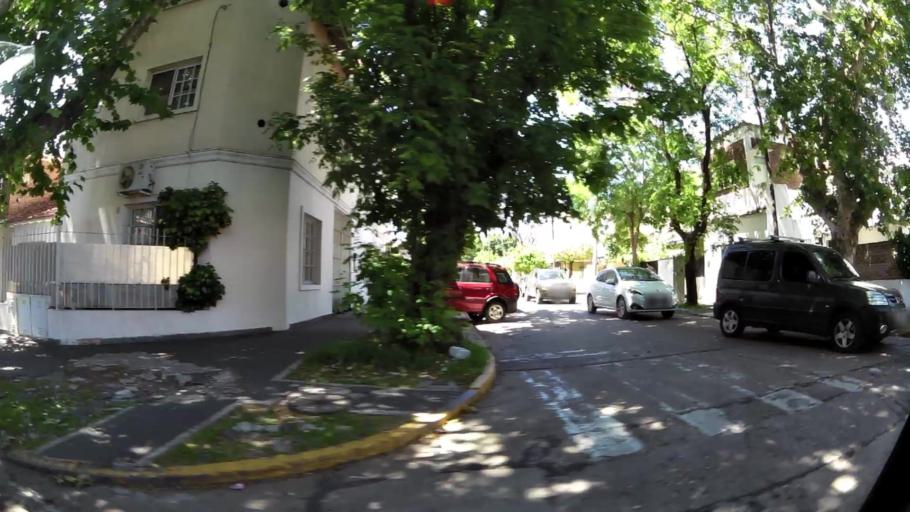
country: AR
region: Buenos Aires
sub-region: Partido de Vicente Lopez
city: Olivos
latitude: -34.5107
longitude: -58.4975
